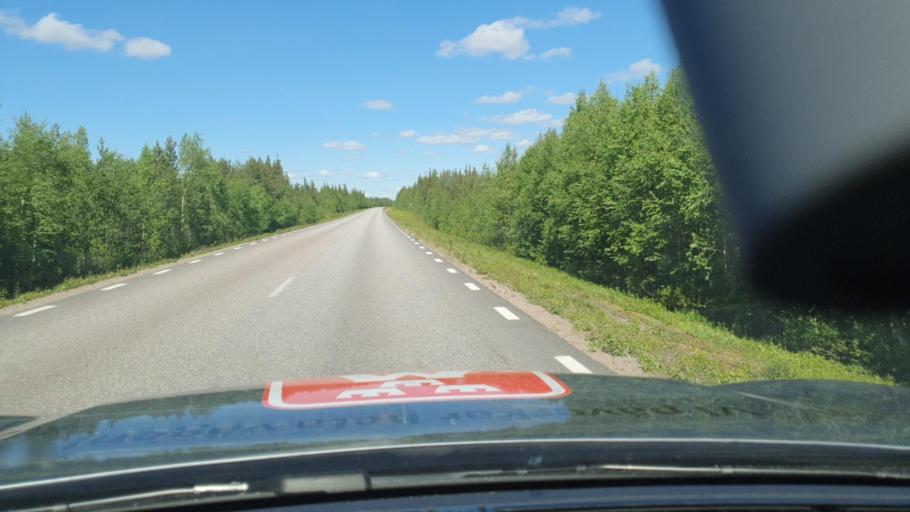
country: SE
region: Norrbotten
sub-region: Overkalix Kommun
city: OEverkalix
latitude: 66.9878
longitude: 22.5975
